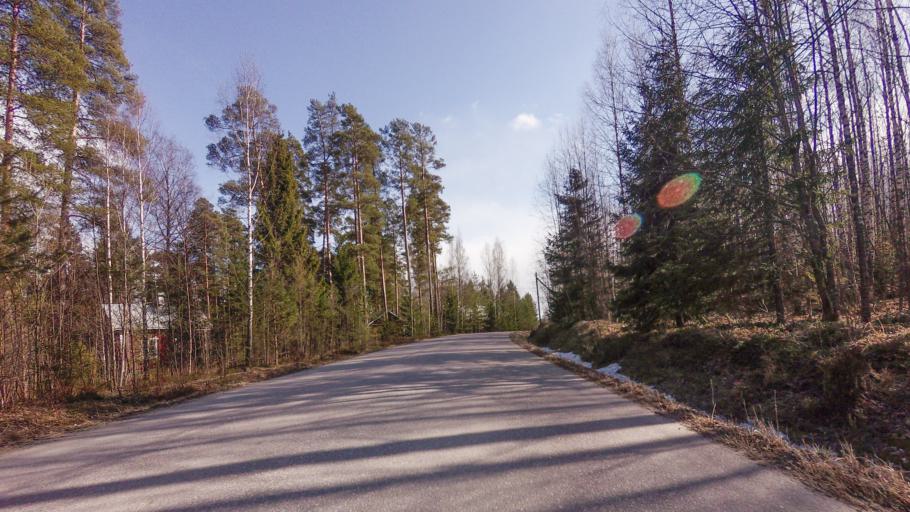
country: FI
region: Varsinais-Suomi
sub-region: Salo
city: Suomusjaervi
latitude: 60.3071
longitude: 23.6467
